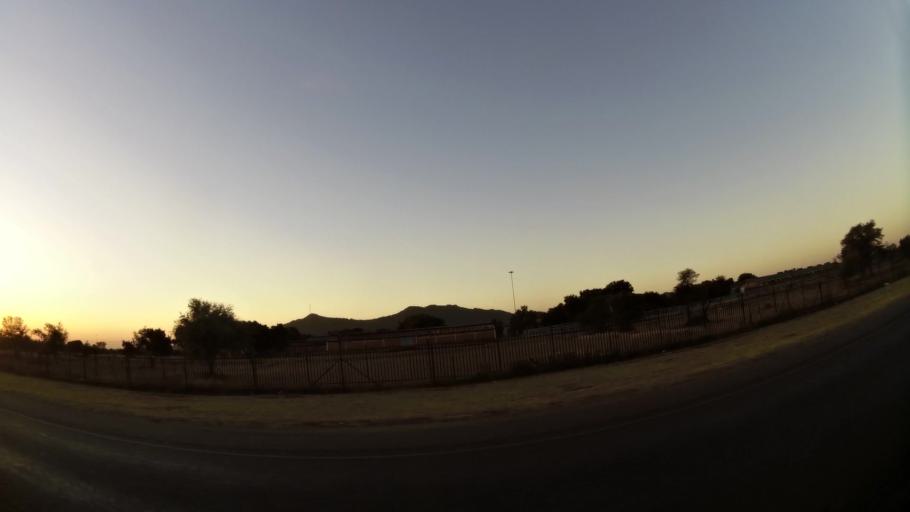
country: ZA
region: North-West
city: Ga-Rankuwa
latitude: -25.6217
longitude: 28.0234
